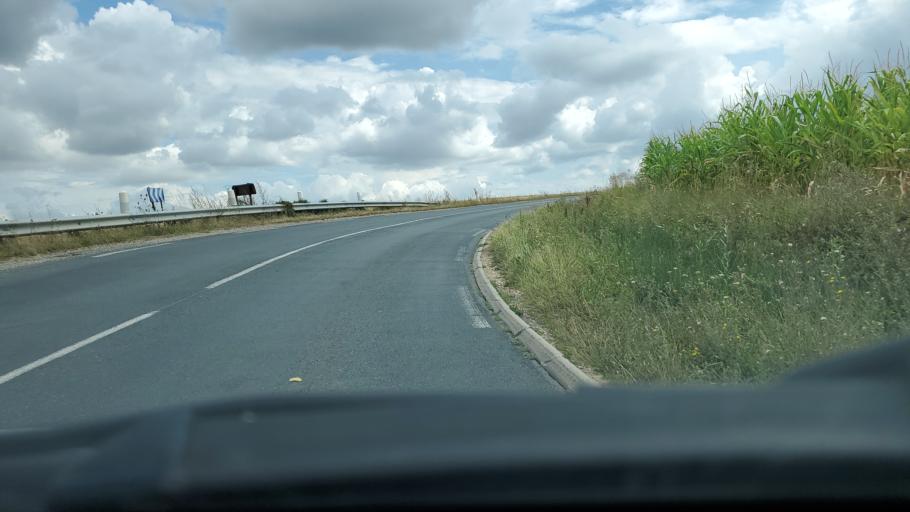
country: FR
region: Ile-de-France
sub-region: Departement de Seine-et-Marne
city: Bouleurs
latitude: 48.8997
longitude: 2.9394
